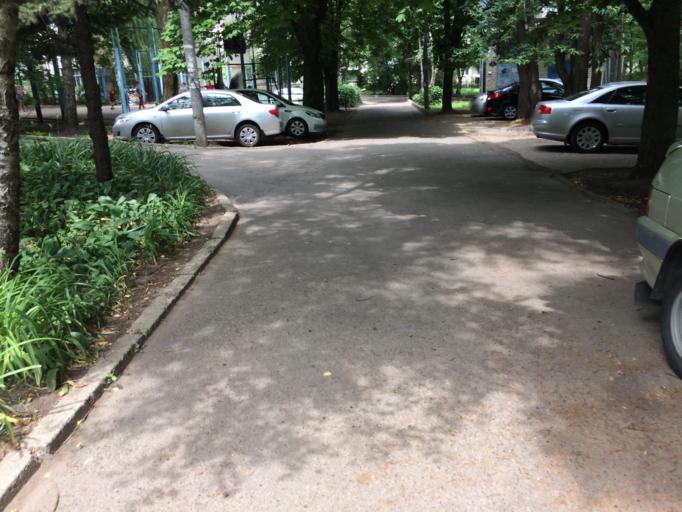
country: RU
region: Stavropol'skiy
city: Stavropol'
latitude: 45.0412
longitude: 41.9546
